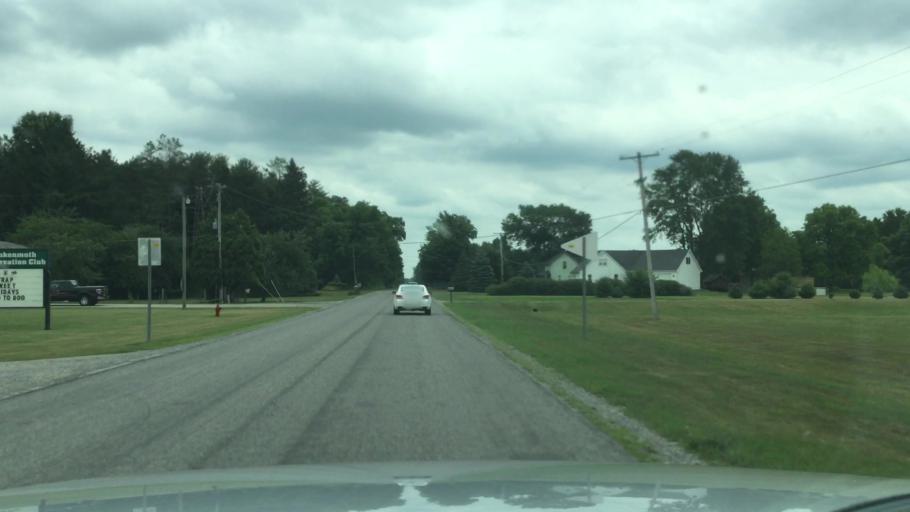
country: US
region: Michigan
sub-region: Saginaw County
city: Frankenmuth
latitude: 43.3217
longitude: -83.7881
